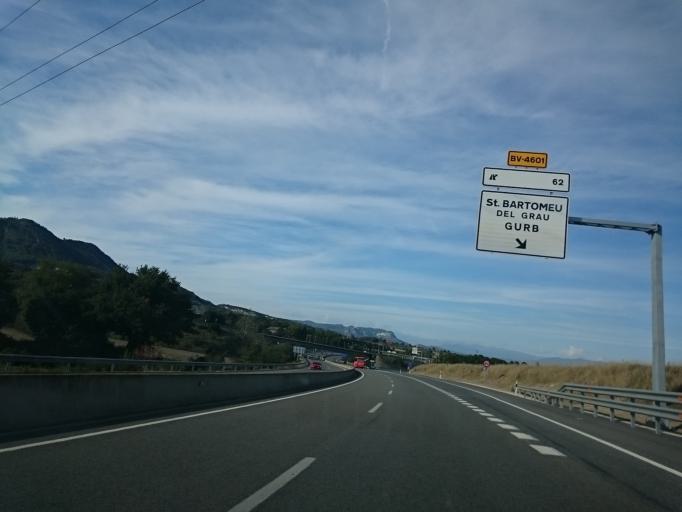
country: ES
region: Catalonia
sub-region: Provincia de Barcelona
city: Gurb
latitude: 41.9382
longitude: 2.2325
